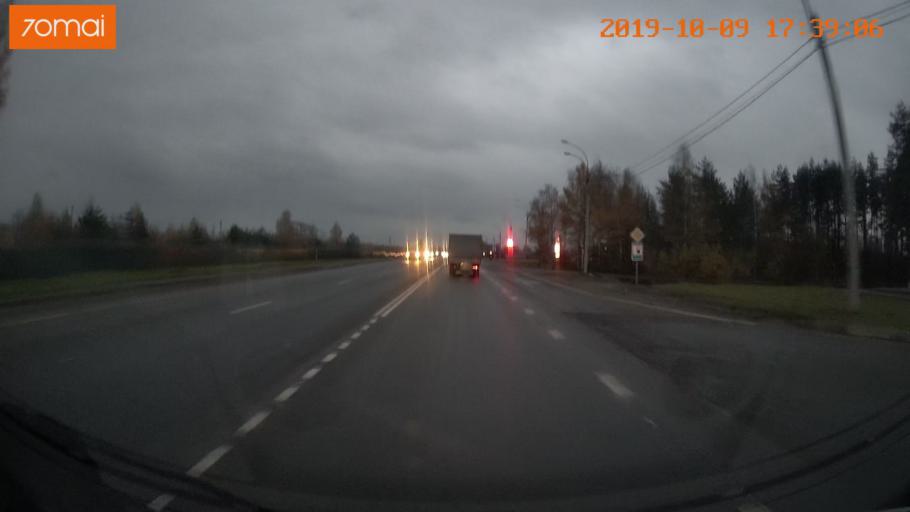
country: RU
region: Ivanovo
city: Bogorodskoye
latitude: 57.0637
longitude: 40.9546
